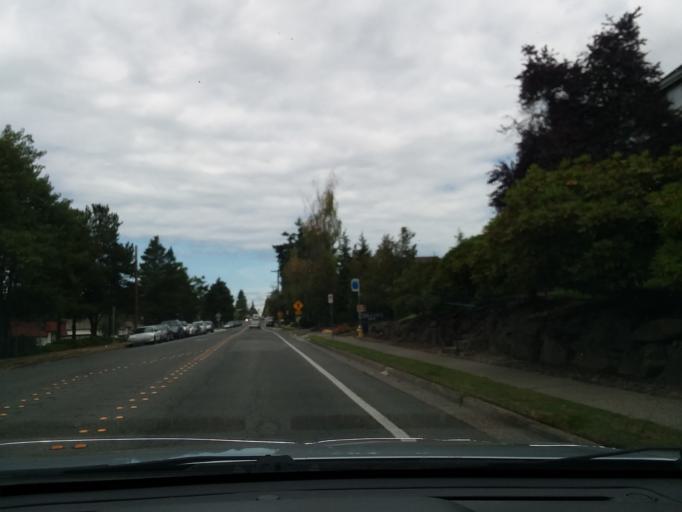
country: US
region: Washington
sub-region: Snohomish County
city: Alderwood Manor
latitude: 47.8180
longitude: -122.2978
